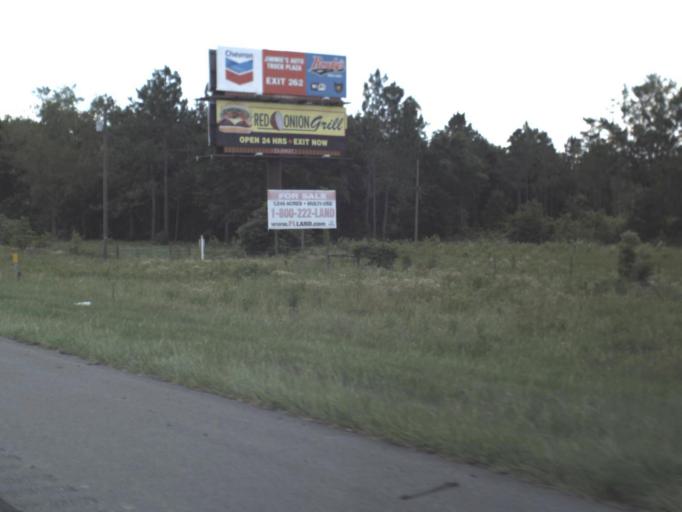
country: US
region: Florida
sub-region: Madison County
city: Madison
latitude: 30.3856
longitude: -83.3177
